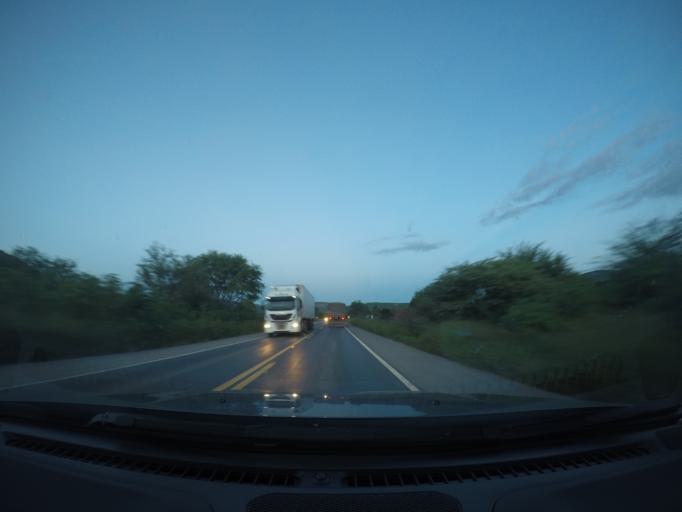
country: BR
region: Bahia
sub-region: Seabra
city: Seabra
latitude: -12.4867
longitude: -41.7263
